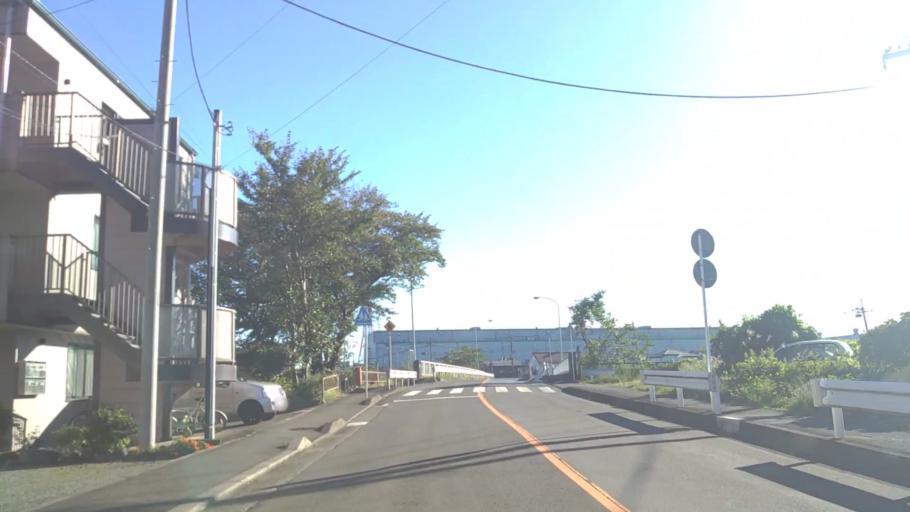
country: JP
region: Kanagawa
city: Atsugi
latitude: 35.4116
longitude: 139.3643
